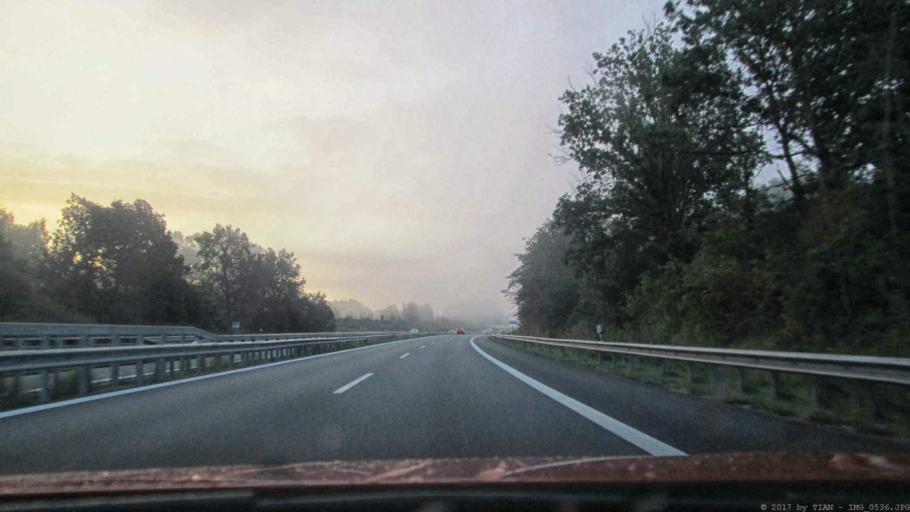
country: DE
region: Hamburg
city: Bergedorf
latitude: 53.4756
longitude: 10.2412
